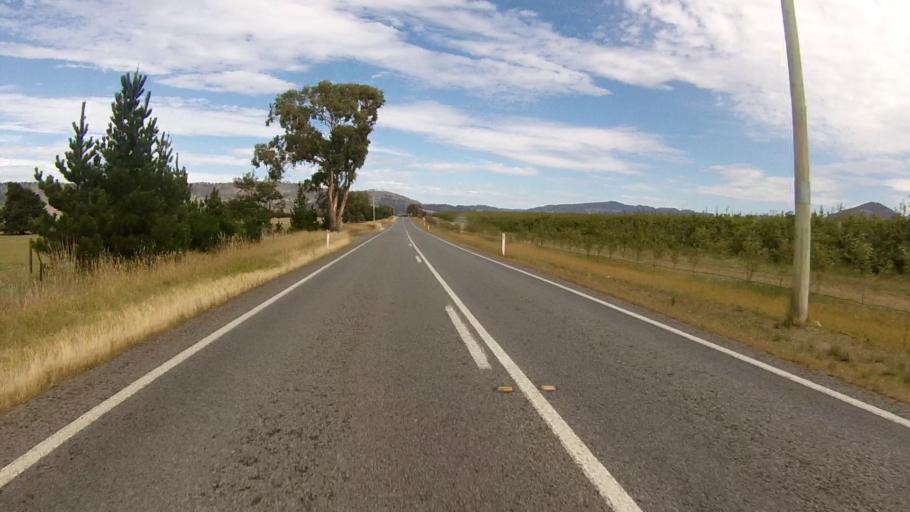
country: AU
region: Tasmania
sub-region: Sorell
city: Sorell
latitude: -42.6897
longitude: 147.4586
